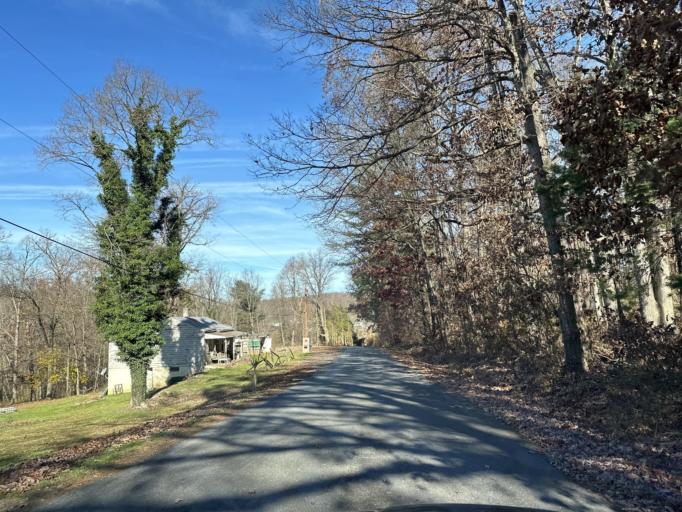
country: US
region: Virginia
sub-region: Rockingham County
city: Bridgewater
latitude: 38.3270
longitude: -78.9627
